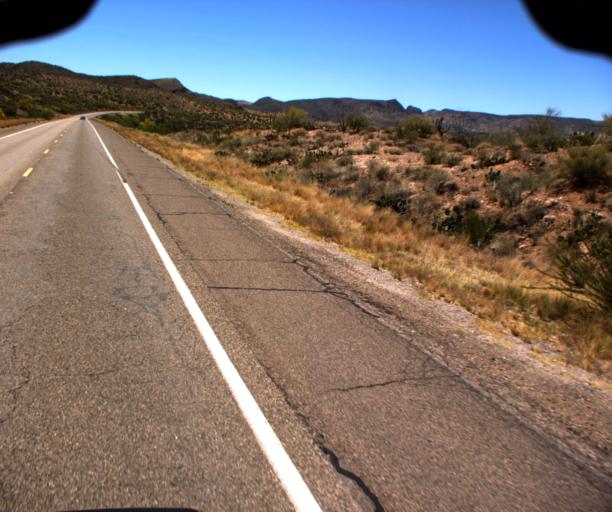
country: US
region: Arizona
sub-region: Pinal County
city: Superior
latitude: 33.2733
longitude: -111.0974
